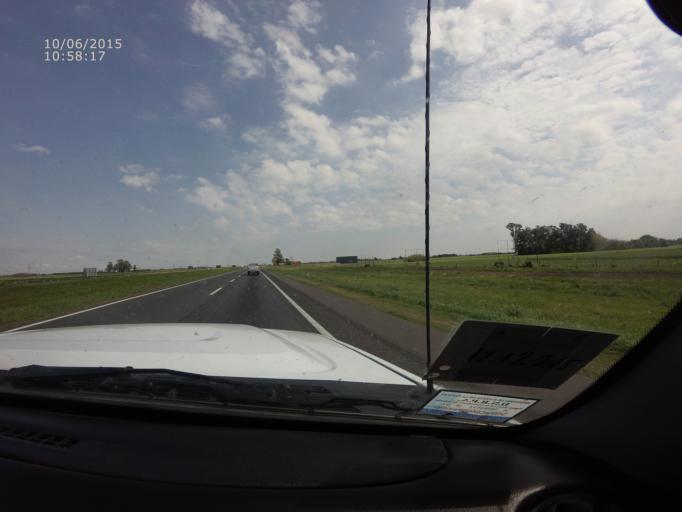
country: AR
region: Santa Fe
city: Villa Constitucion
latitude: -33.2941
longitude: -60.3655
